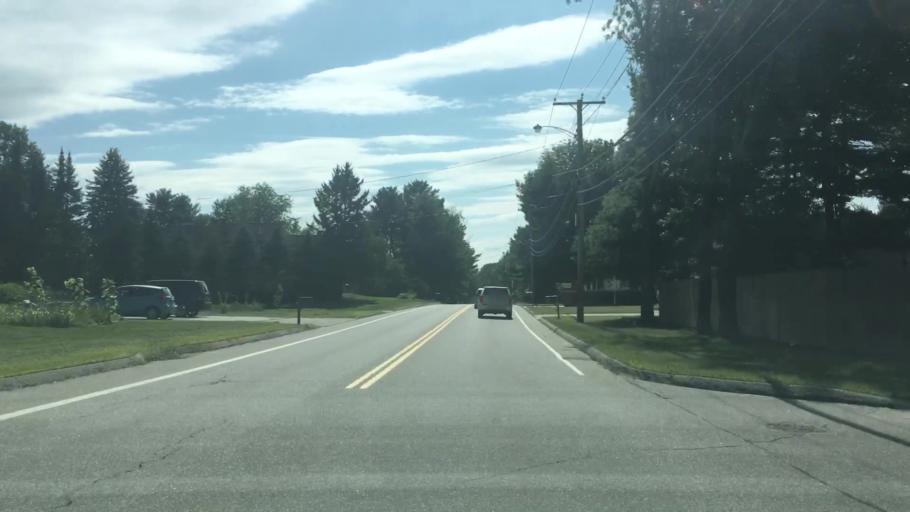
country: US
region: Maine
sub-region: Androscoggin County
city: Lewiston
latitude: 44.0865
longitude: -70.1668
